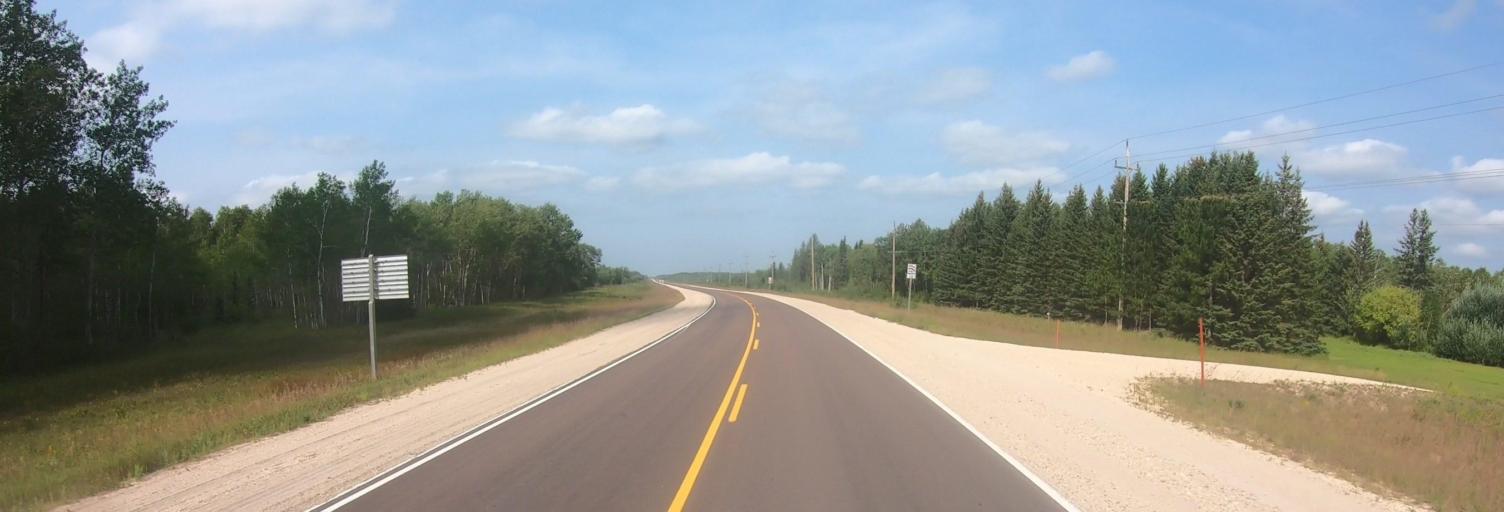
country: CA
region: Manitoba
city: La Broquerie
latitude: 49.2669
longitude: -96.3698
